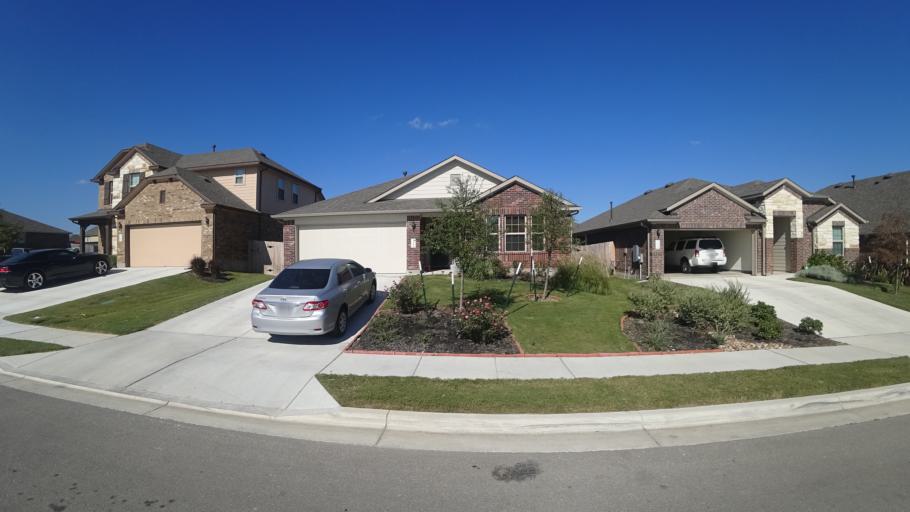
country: US
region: Texas
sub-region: Travis County
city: Manor
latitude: 30.3565
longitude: -97.6040
